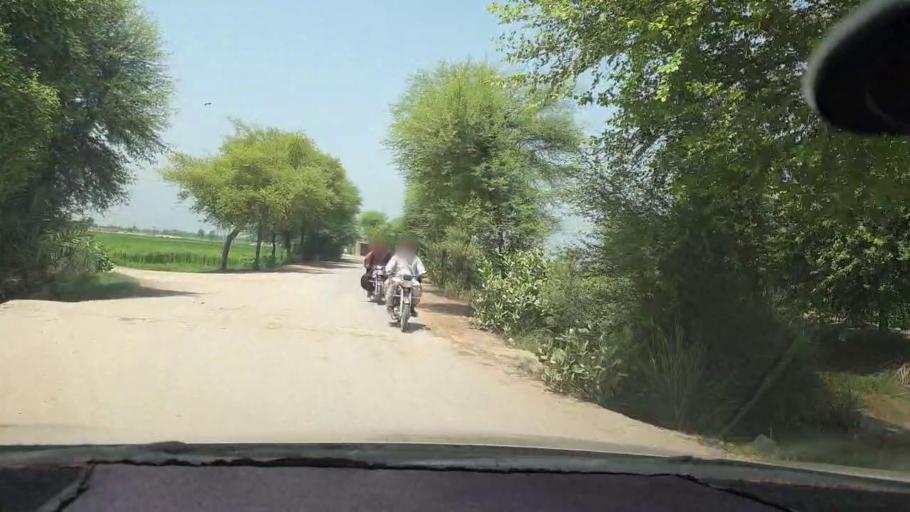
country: PK
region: Sindh
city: Kambar
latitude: 27.6375
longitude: 67.9779
